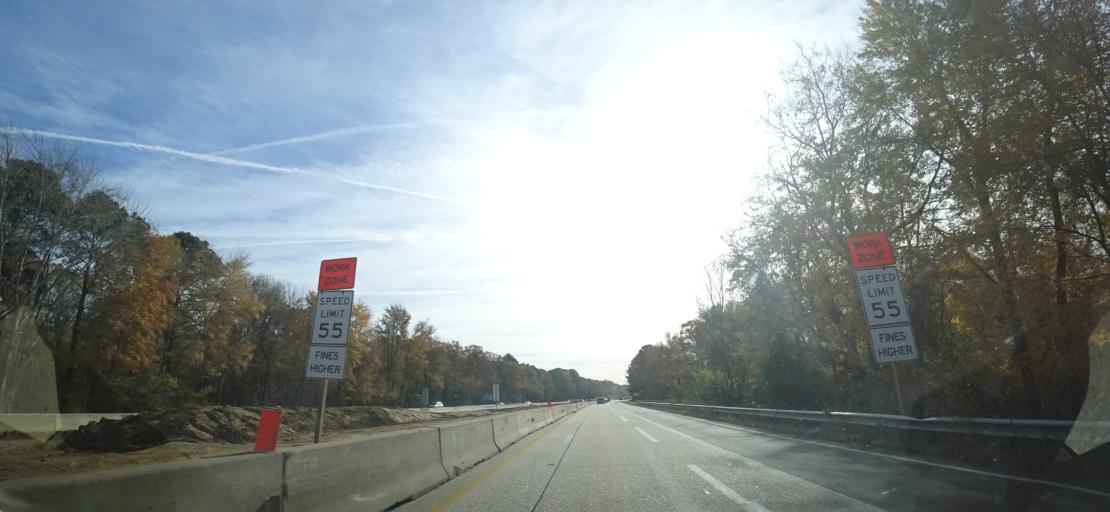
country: US
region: Virginia
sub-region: York County
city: Yorktown
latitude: 37.2042
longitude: -76.5737
